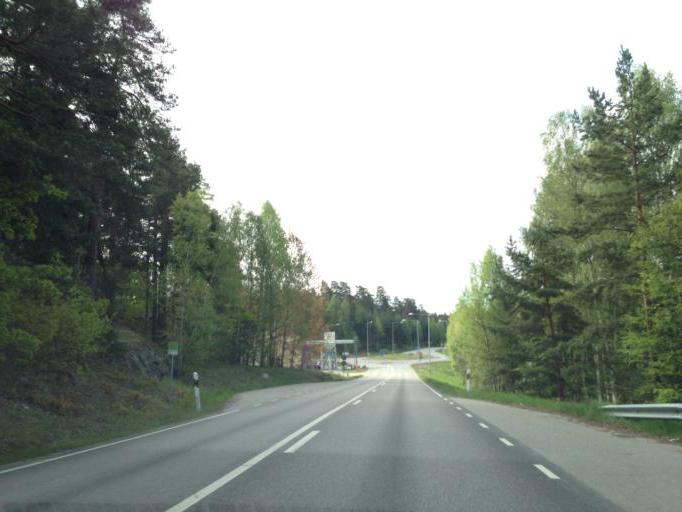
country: SE
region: Soedermanland
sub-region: Flens Kommun
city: Malmkoping
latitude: 59.0685
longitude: 16.8182
